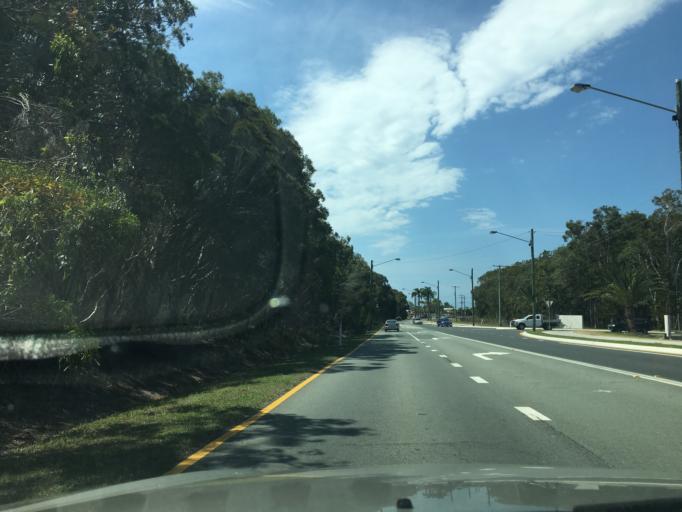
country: AU
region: Queensland
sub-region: Moreton Bay
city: Bongaree
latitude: -27.0776
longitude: 153.1369
